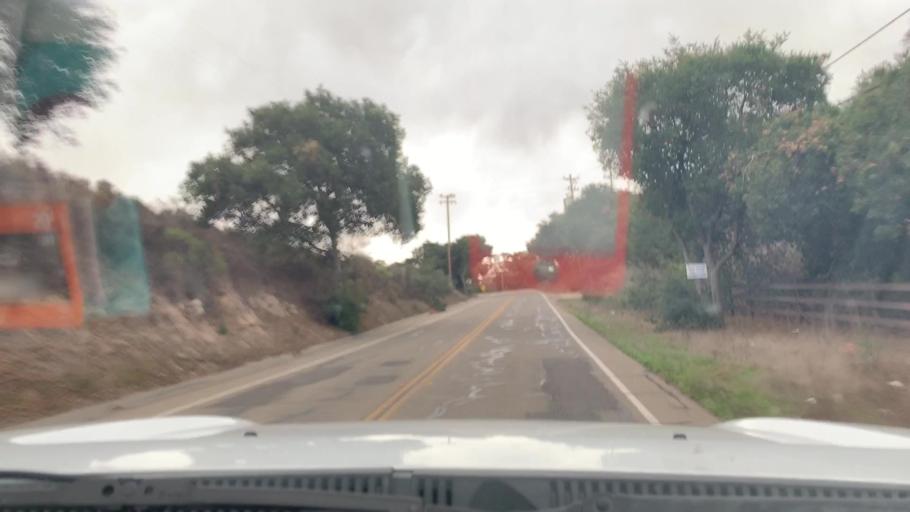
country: US
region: California
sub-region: San Luis Obispo County
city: Nipomo
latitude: 35.0758
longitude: -120.5238
